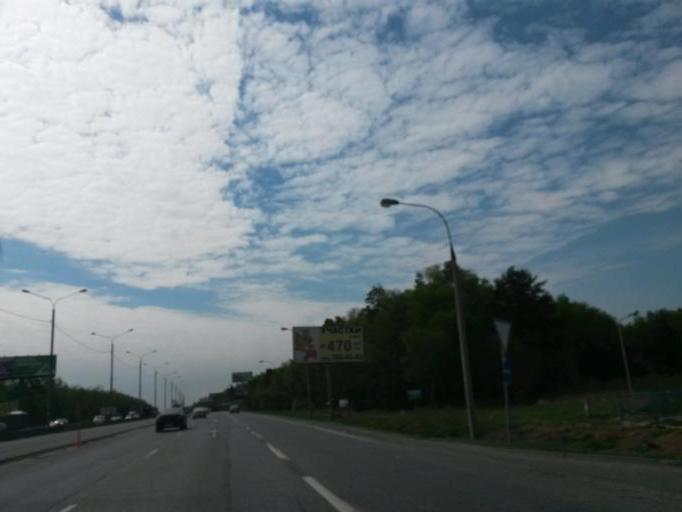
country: RU
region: Moskovskaya
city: Shcherbinka
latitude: 55.5205
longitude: 37.6086
